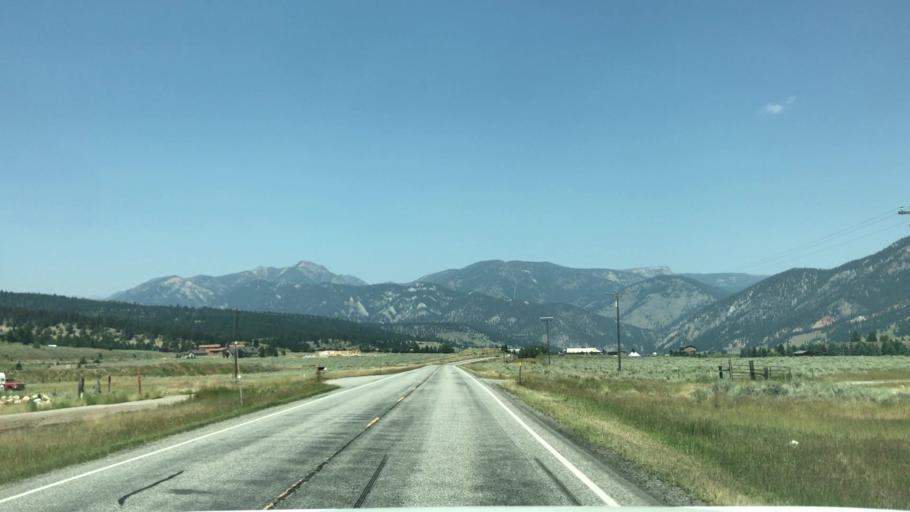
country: US
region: Montana
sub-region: Gallatin County
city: Big Sky
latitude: 45.2168
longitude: -111.2492
